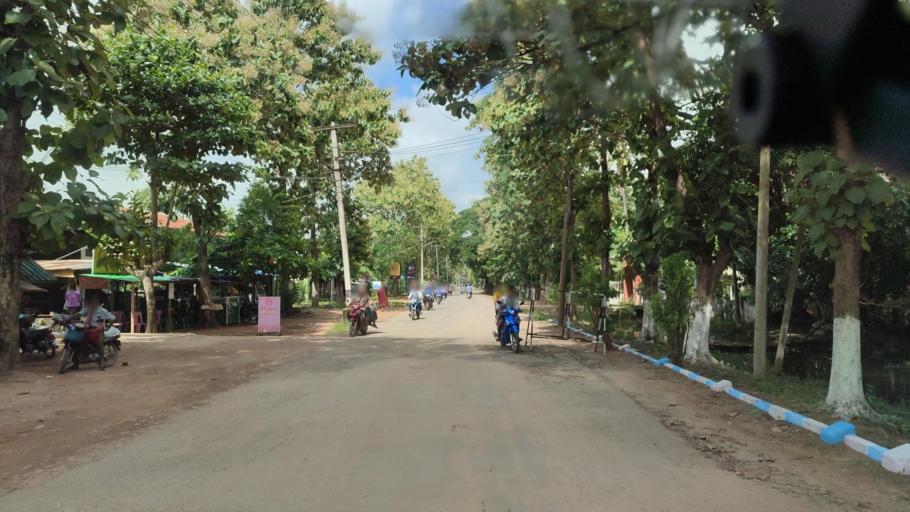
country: MM
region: Bago
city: Letpandan
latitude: 17.9796
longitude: 95.7159
